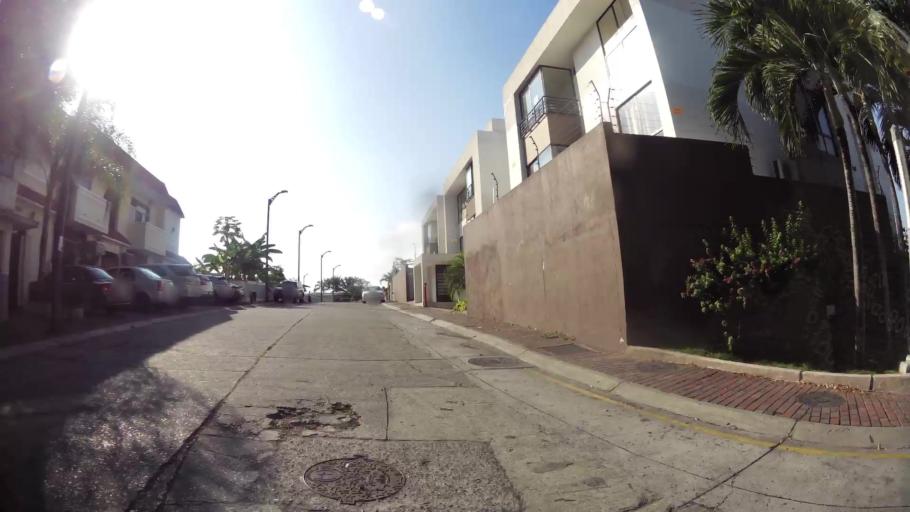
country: EC
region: Guayas
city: Guayaquil
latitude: -2.1656
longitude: -79.9043
